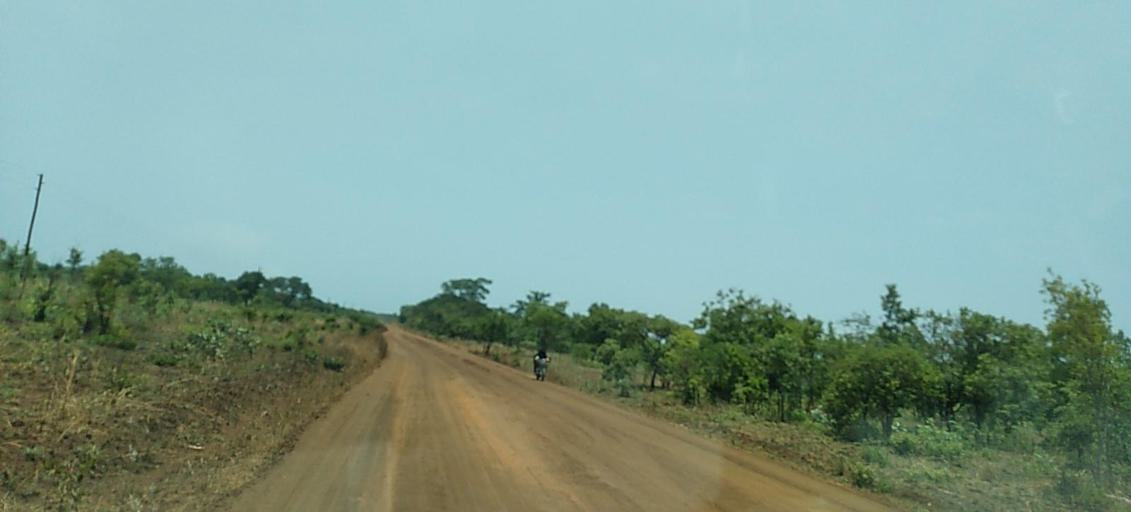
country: ZM
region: Copperbelt
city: Mpongwe
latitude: -13.6993
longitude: 27.8666
